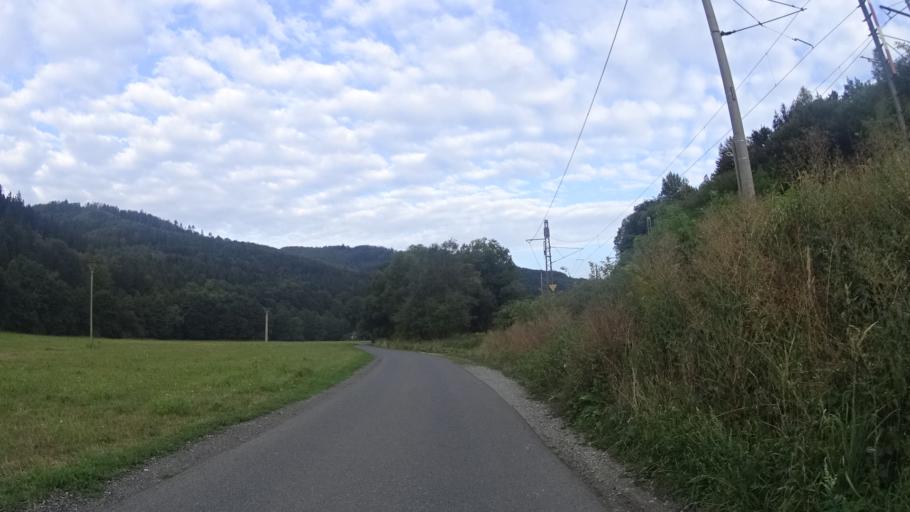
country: CZ
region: Olomoucky
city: Zabreh
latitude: 49.8661
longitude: 16.7985
